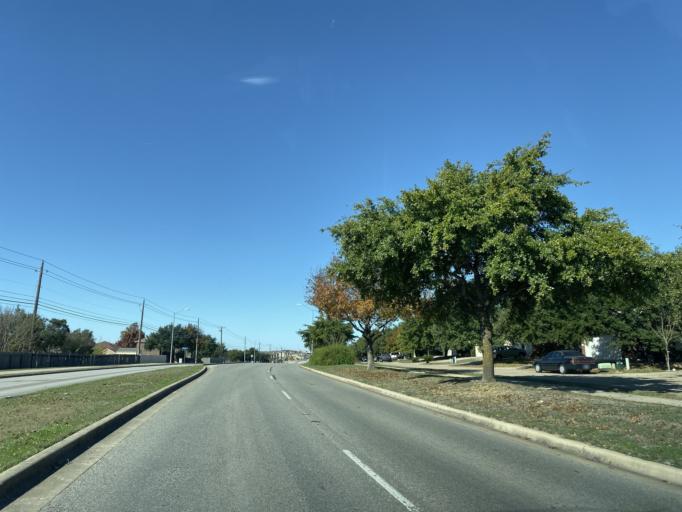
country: US
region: Texas
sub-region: Travis County
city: Windemere
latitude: 30.4717
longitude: -97.6518
